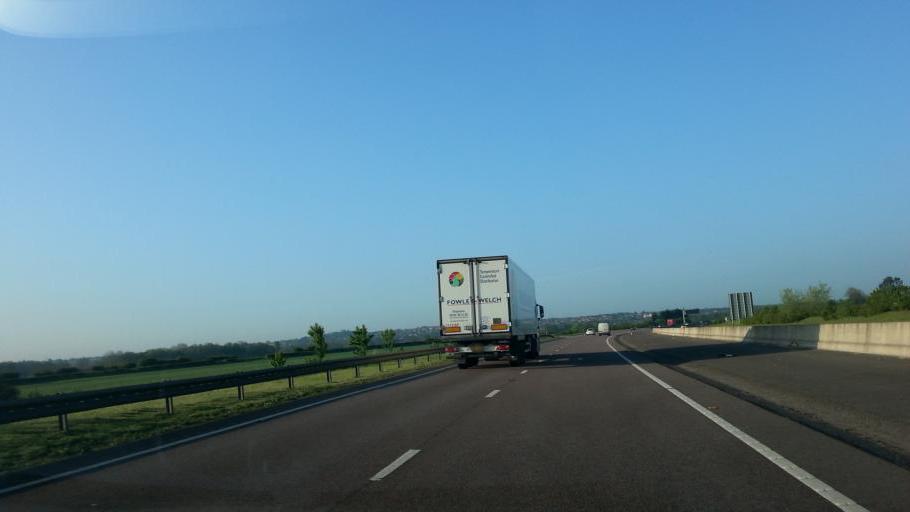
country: GB
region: England
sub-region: Nottinghamshire
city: East Bridgford
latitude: 52.9650
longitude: -0.9646
